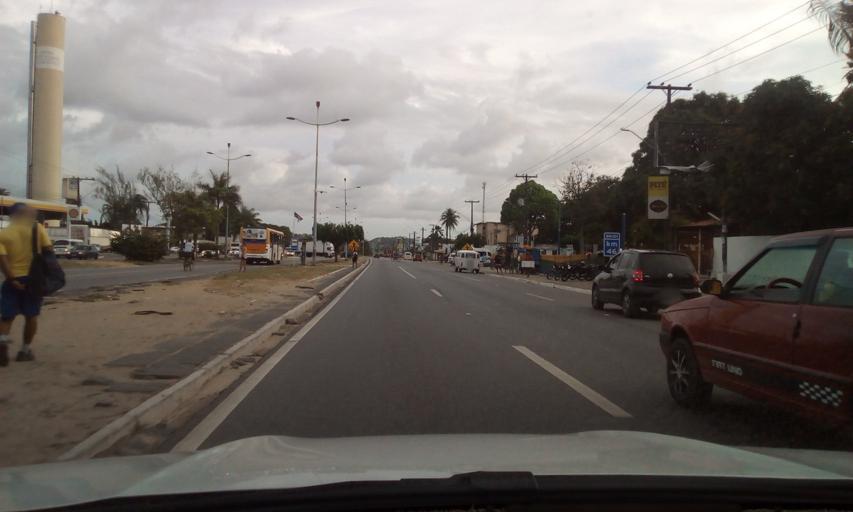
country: BR
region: Pernambuco
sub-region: Abreu E Lima
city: Abreu e Lima
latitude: -7.8738
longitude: -34.9062
